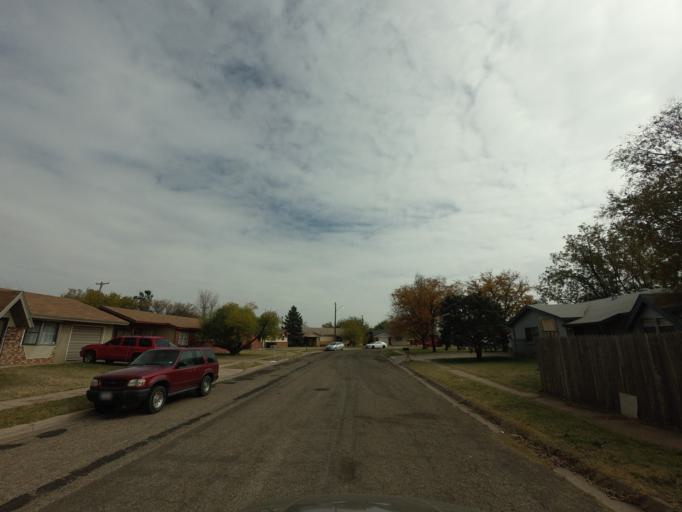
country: US
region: New Mexico
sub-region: Curry County
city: Clovis
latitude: 34.4291
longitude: -103.2222
